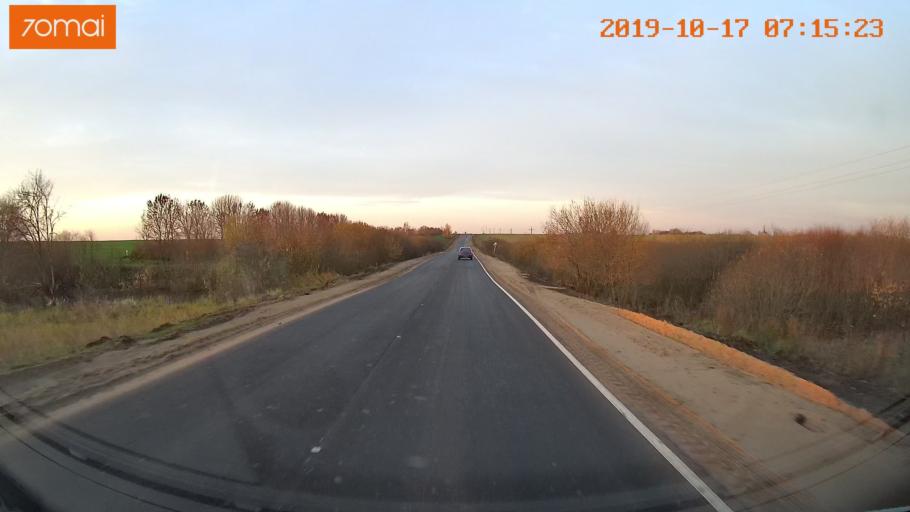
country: RU
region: Vladimir
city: Suzdal'
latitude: 56.3812
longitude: 40.2687
